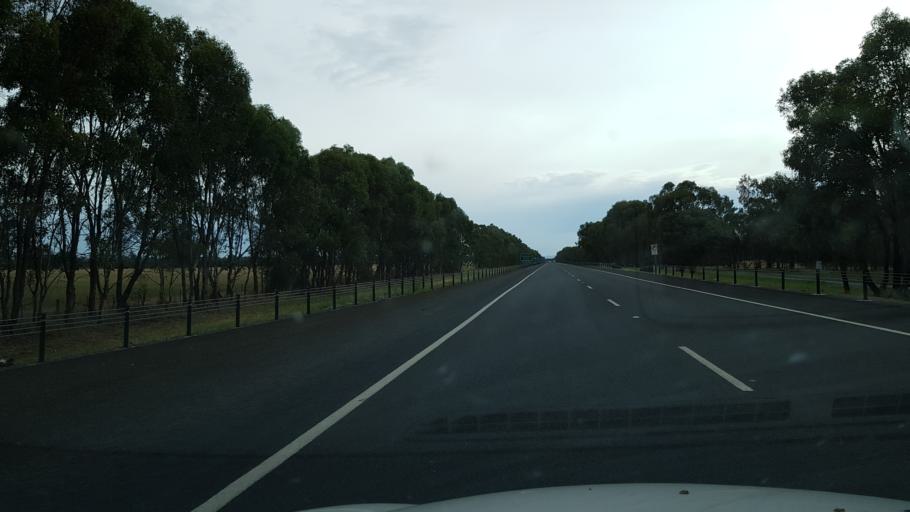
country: AU
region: Victoria
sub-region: Wangaratta
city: Wangaratta
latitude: -36.2872
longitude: 146.3937
